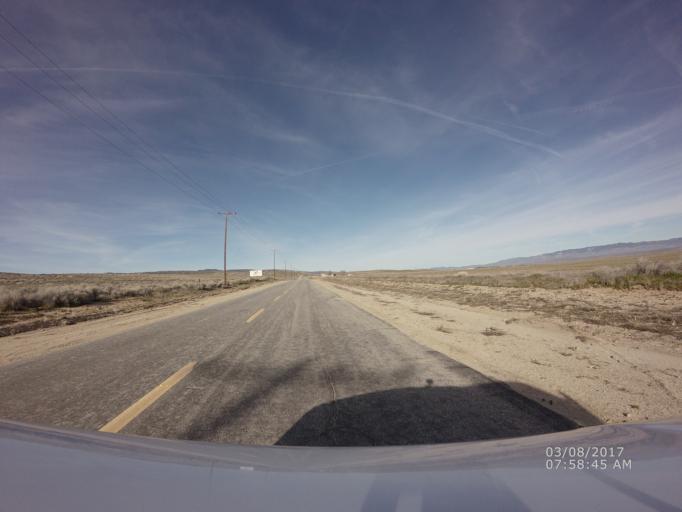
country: US
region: California
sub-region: Los Angeles County
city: Green Valley
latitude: 34.7246
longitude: -118.4071
